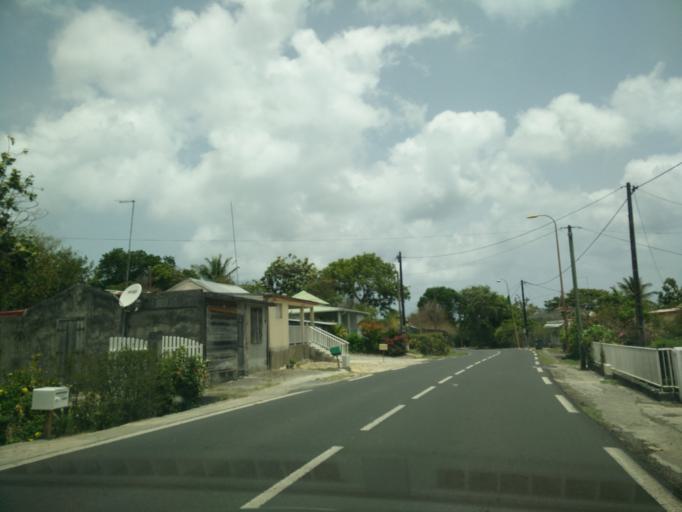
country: GP
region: Guadeloupe
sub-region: Guadeloupe
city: Port-Louis
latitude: 16.4151
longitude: -61.5249
